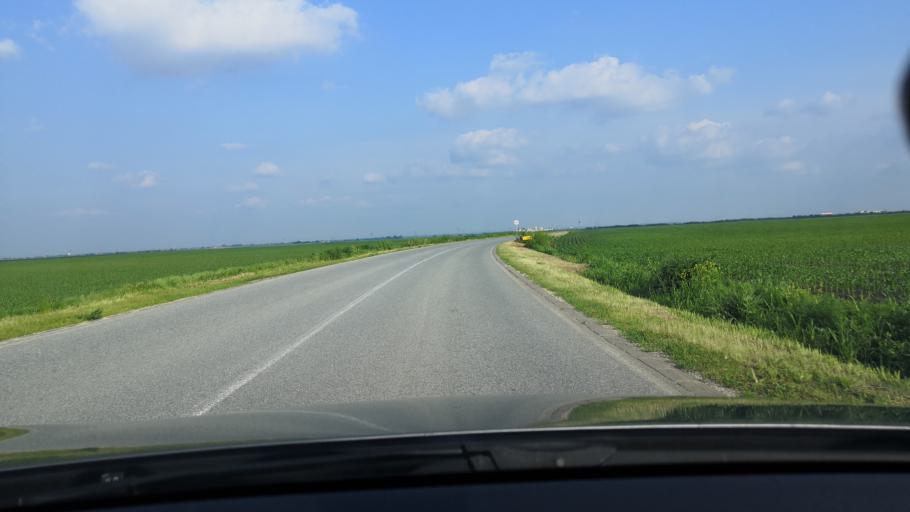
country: RS
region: Autonomna Pokrajina Vojvodina
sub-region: Sremski Okrug
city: Ingija
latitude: 45.0871
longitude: 20.1090
